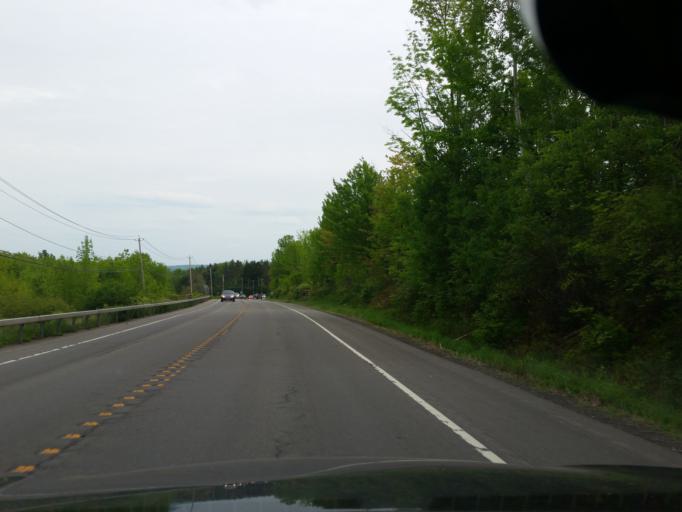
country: US
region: New York
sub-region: Chautauqua County
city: Lakewood
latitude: 42.1380
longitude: -79.3991
